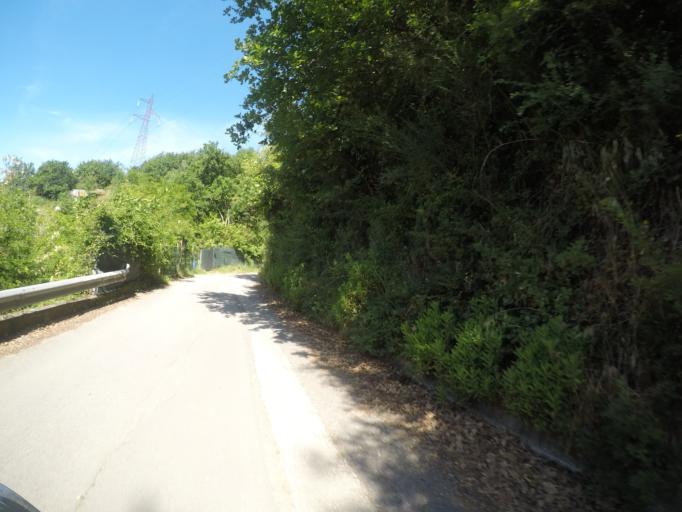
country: IT
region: Tuscany
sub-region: Provincia di Massa-Carrara
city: Massa
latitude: 44.0501
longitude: 10.1171
